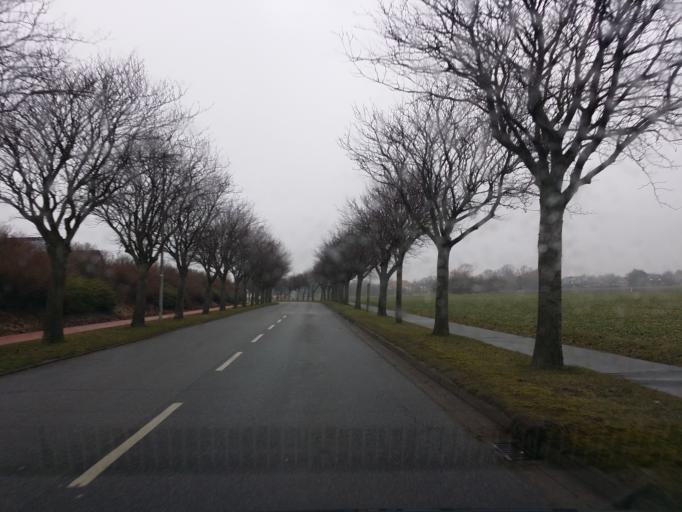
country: DE
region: Schleswig-Holstein
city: Burg auf Fehmarn
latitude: 54.4279
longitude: 11.2026
